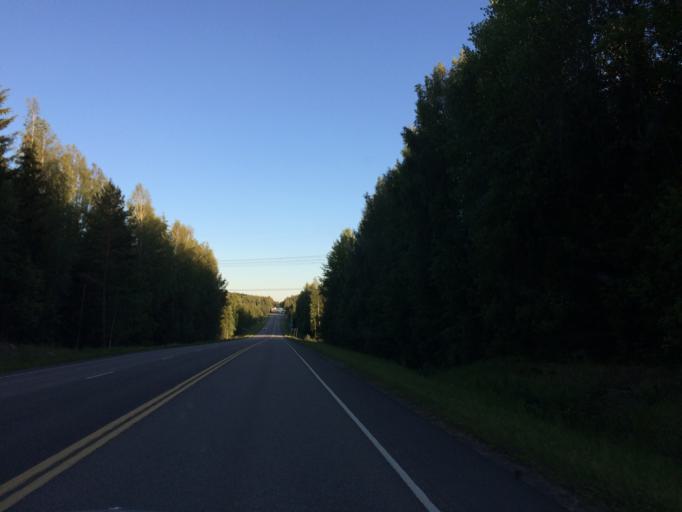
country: FI
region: Haeme
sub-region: Riihimaeki
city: Riihimaeki
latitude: 60.7576
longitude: 24.7185
